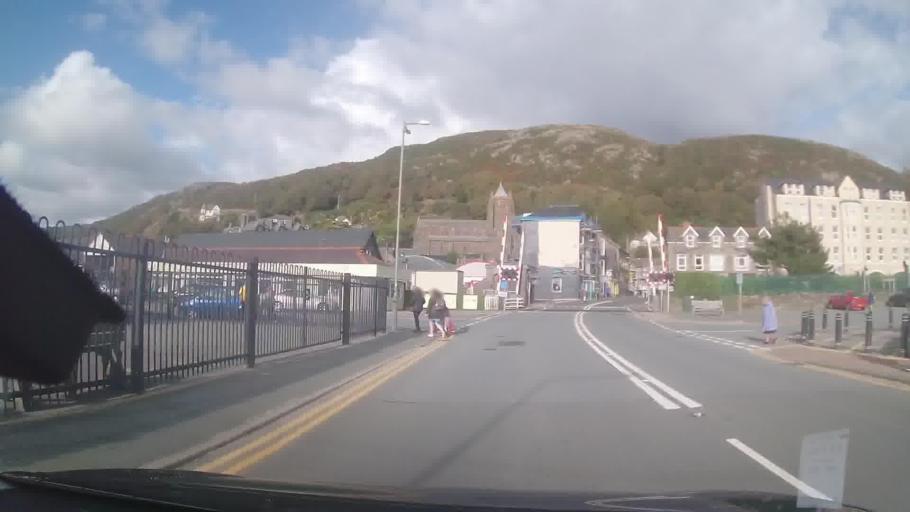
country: GB
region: Wales
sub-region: Gwynedd
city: Barmouth
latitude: 52.7217
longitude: -4.0574
